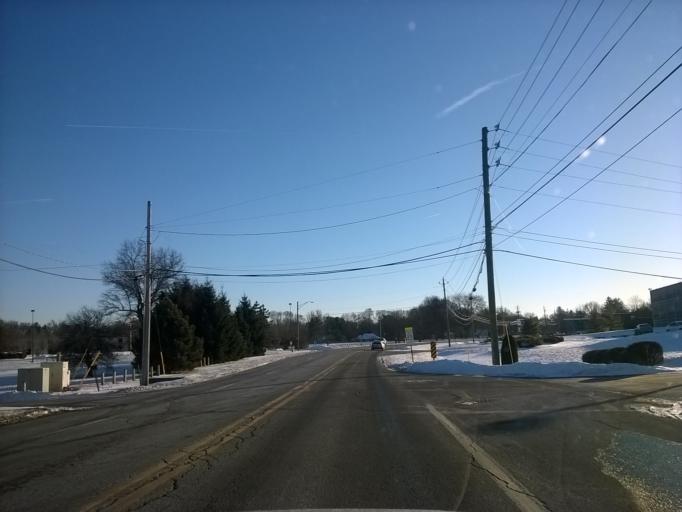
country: US
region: Indiana
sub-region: Marion County
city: Meridian Hills
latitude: 39.9111
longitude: -86.1340
